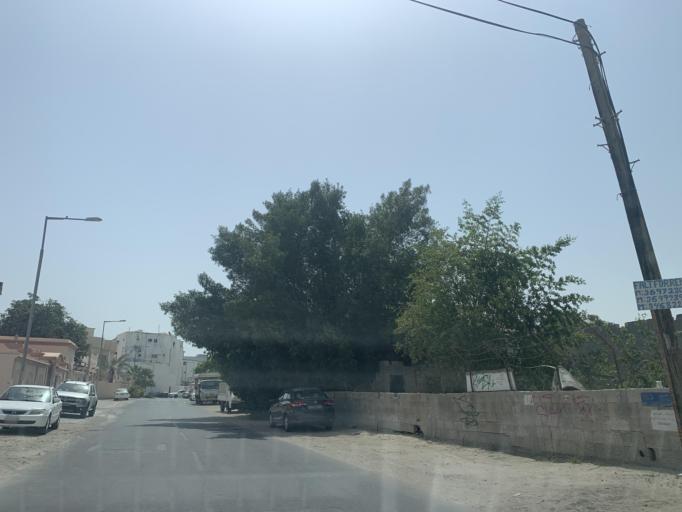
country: BH
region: Northern
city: Madinat `Isa
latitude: 26.1863
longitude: 50.5444
